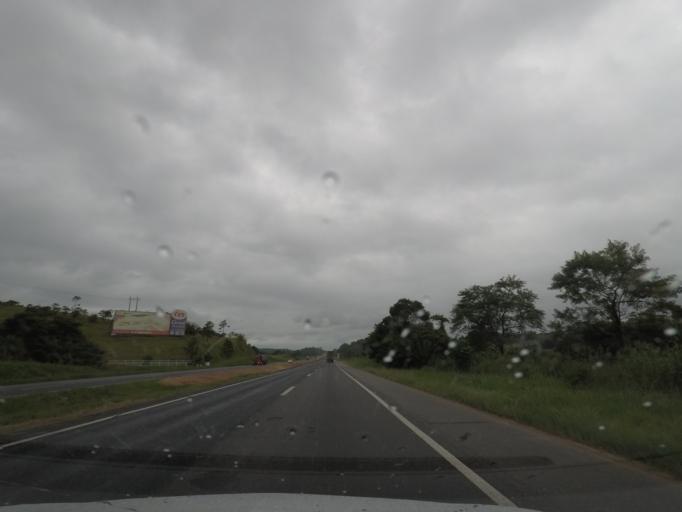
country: BR
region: Sao Paulo
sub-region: Registro
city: Registro
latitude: -24.4287
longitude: -47.7848
